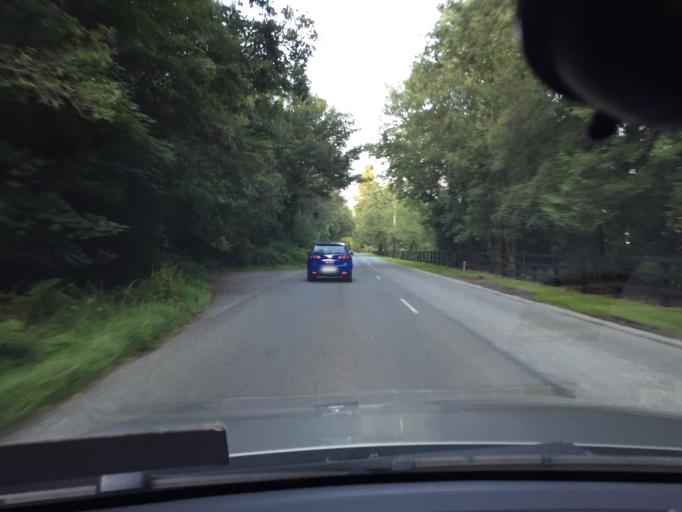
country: IE
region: Leinster
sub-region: Wicklow
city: Rathdrum
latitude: 53.0228
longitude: -6.2714
